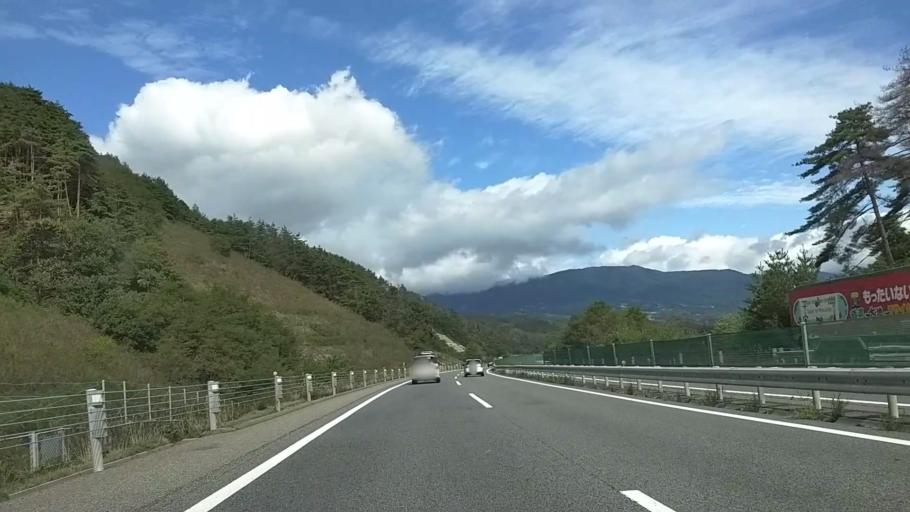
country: JP
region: Nagano
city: Hotaka
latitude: 36.4032
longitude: 138.0007
